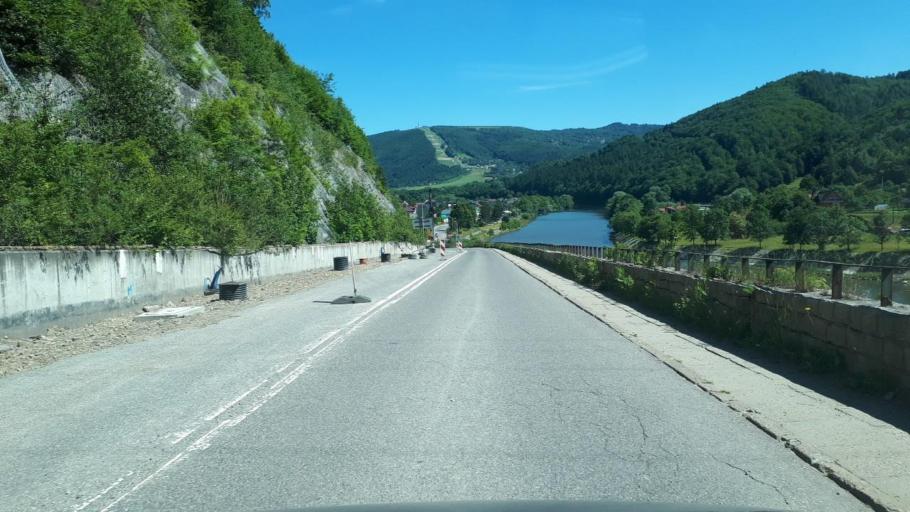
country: PL
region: Silesian Voivodeship
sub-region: Powiat zywiecki
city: Czernichow
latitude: 49.7478
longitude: 19.2056
